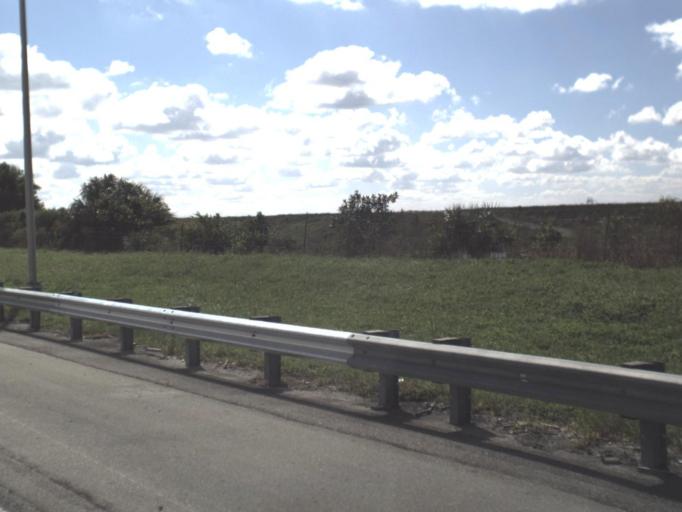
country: US
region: Florida
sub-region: Broward County
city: Coral Springs
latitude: 26.2646
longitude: -80.2974
